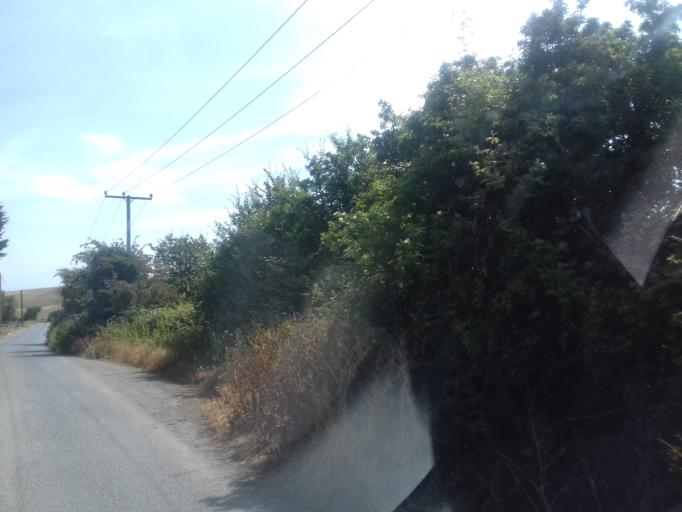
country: IE
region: Leinster
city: Lusk
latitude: 53.5130
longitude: -6.1528
